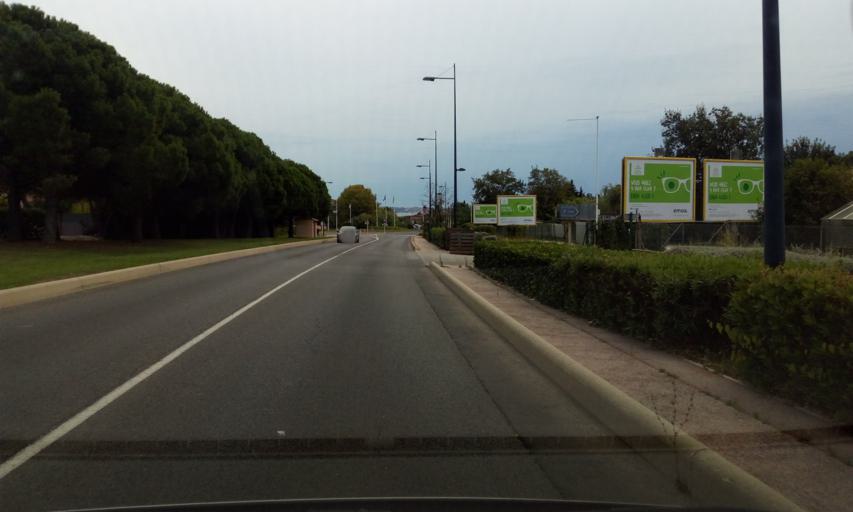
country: FR
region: Provence-Alpes-Cote d'Azur
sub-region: Departement du Var
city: Carqueiranne
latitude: 43.0970
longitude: 6.0682
